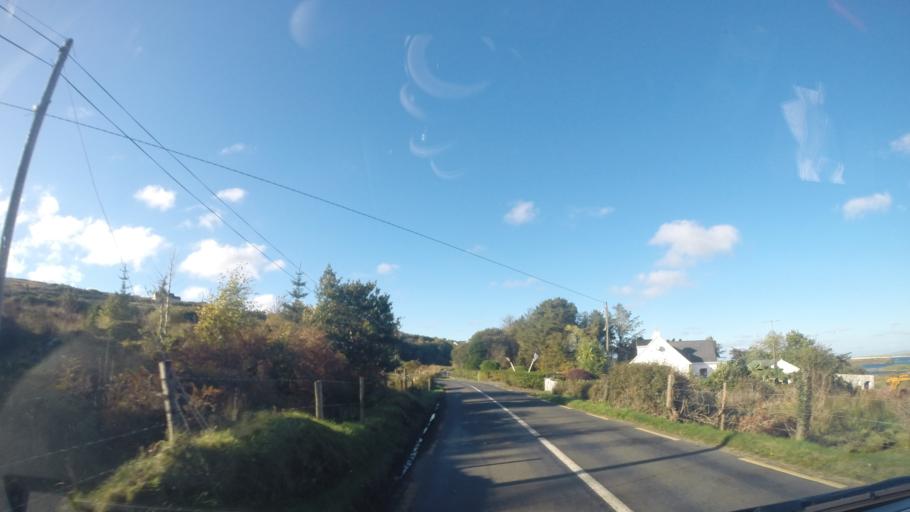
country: IE
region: Ulster
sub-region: County Donegal
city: Dungloe
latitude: 54.8340
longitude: -8.3511
